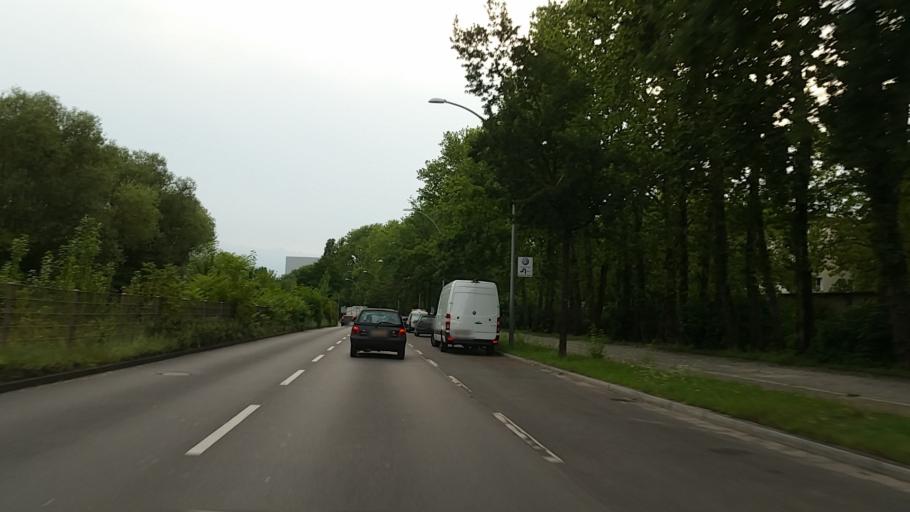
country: DE
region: Berlin
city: Haselhorst
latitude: 52.5394
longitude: 13.2373
